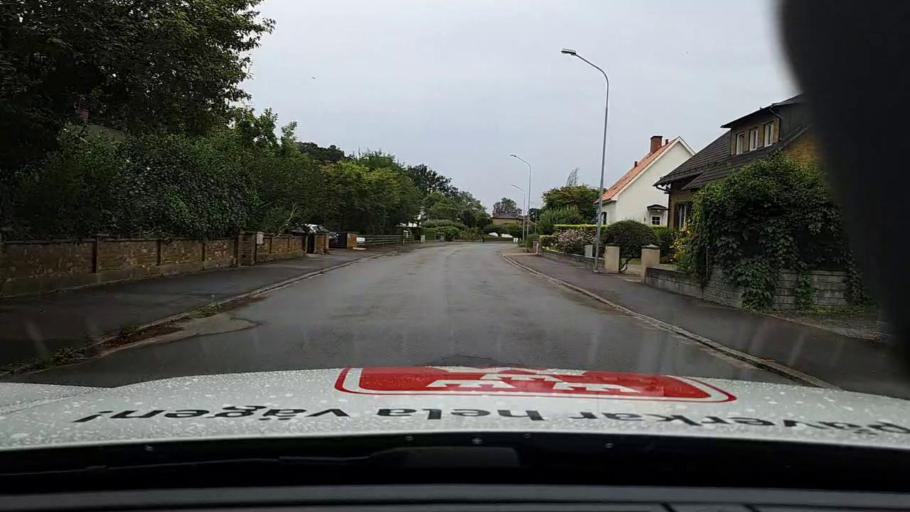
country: SE
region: Skane
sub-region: Hassleholms Kommun
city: Hassleholm
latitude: 56.1681
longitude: 13.7737
